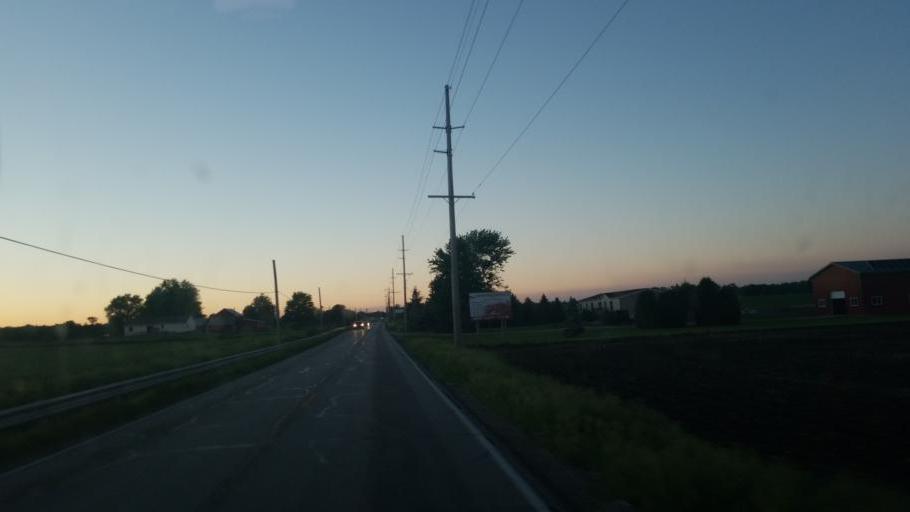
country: US
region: Indiana
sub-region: Elkhart County
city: Nappanee
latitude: 41.4179
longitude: -86.0012
